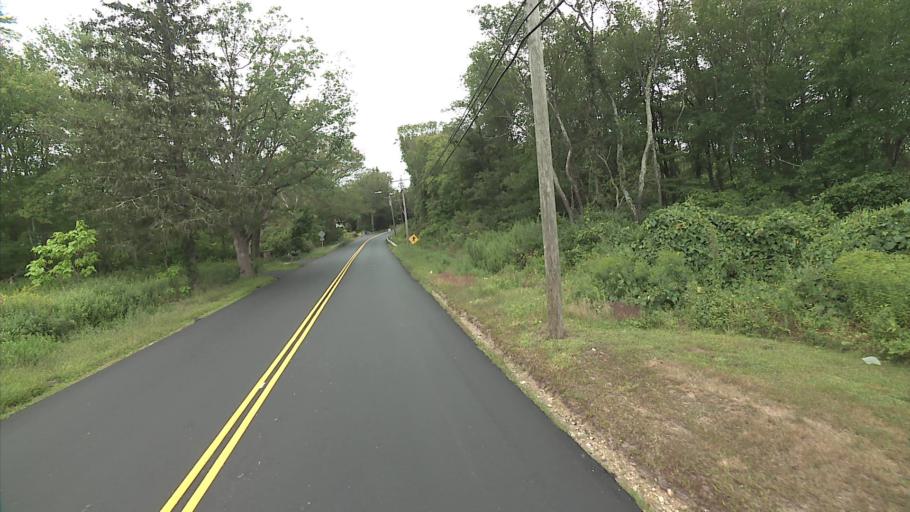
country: US
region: Connecticut
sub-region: New London County
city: Colchester
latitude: 41.5840
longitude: -72.3371
